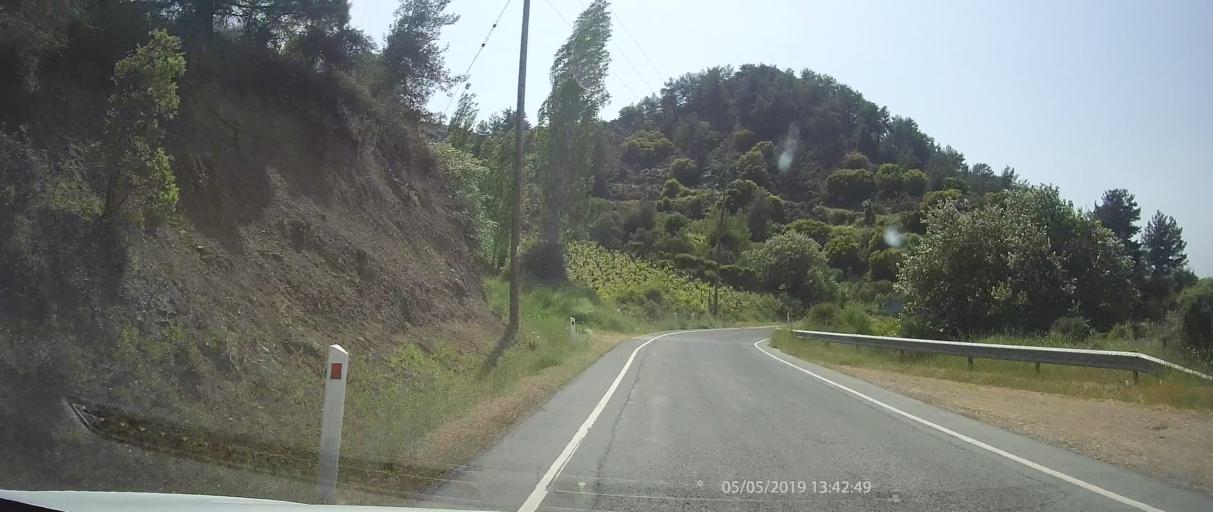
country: CY
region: Limassol
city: Pachna
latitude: 34.8726
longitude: 32.8039
